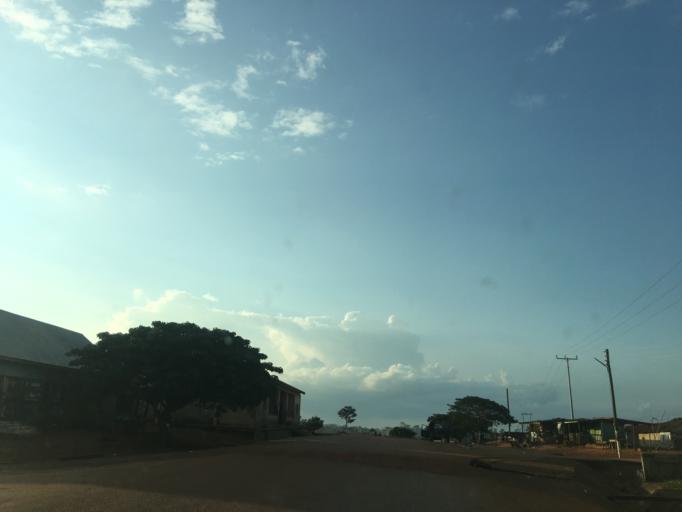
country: GH
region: Western
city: Bibiani
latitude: 6.5676
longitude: -2.3719
